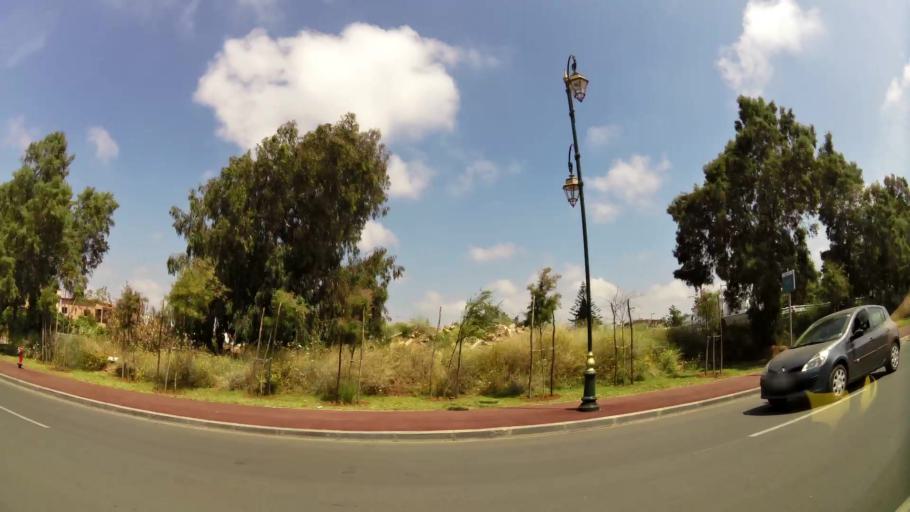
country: MA
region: Rabat-Sale-Zemmour-Zaer
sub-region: Skhirate-Temara
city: Temara
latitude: 33.9596
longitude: -6.8852
